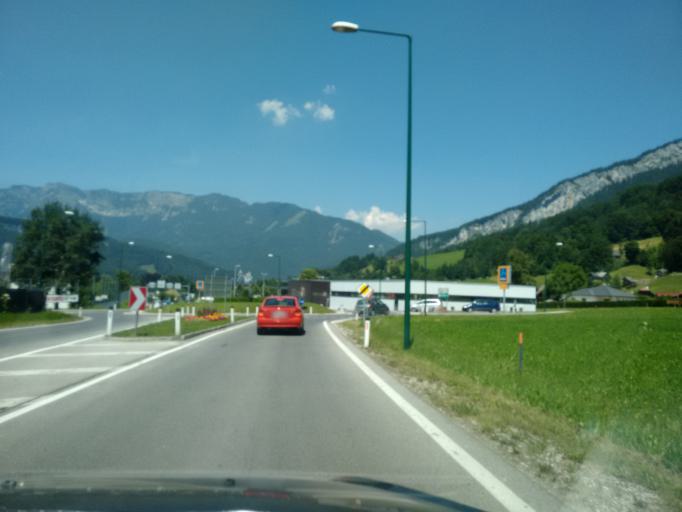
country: AT
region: Upper Austria
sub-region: Politischer Bezirk Gmunden
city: Bad Goisern
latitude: 47.6402
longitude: 13.6212
